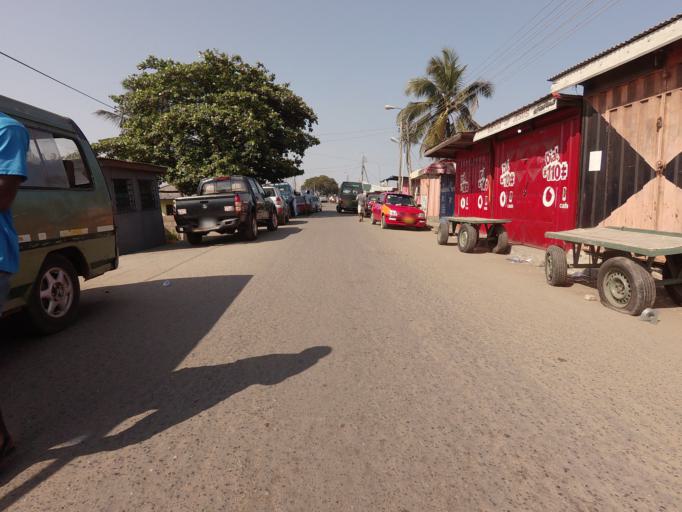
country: GH
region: Greater Accra
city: Teshi Old Town
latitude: 5.5786
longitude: -0.1046
